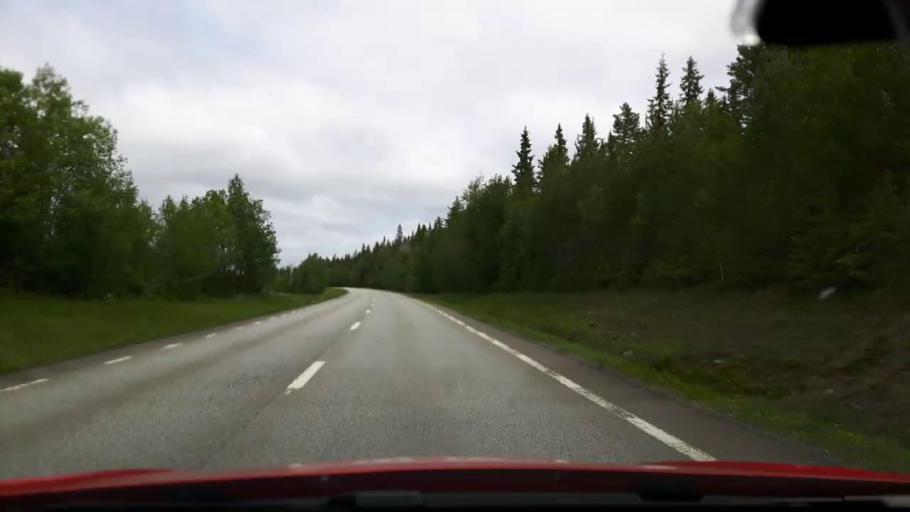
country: SE
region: Jaemtland
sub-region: Krokoms Kommun
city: Krokom
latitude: 63.4730
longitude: 14.5021
